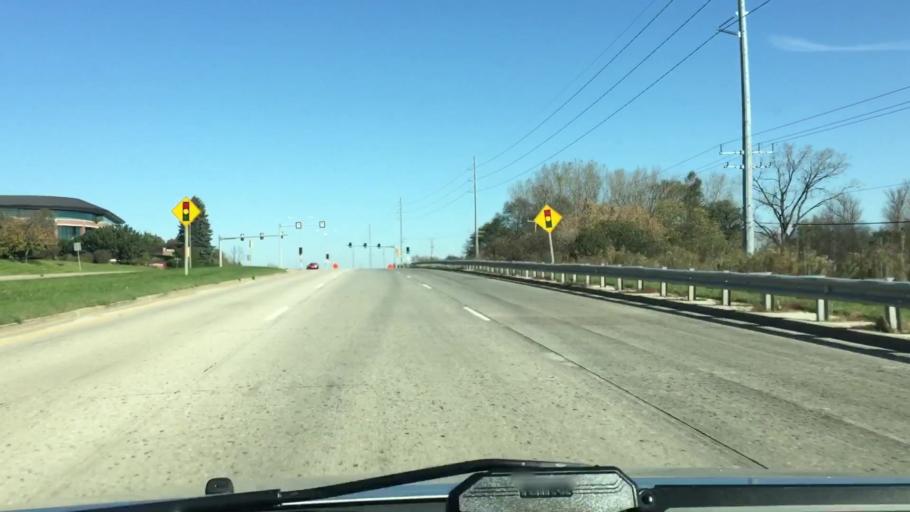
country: US
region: Wisconsin
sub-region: Waukesha County
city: Waukesha
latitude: 43.0525
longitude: -88.2065
